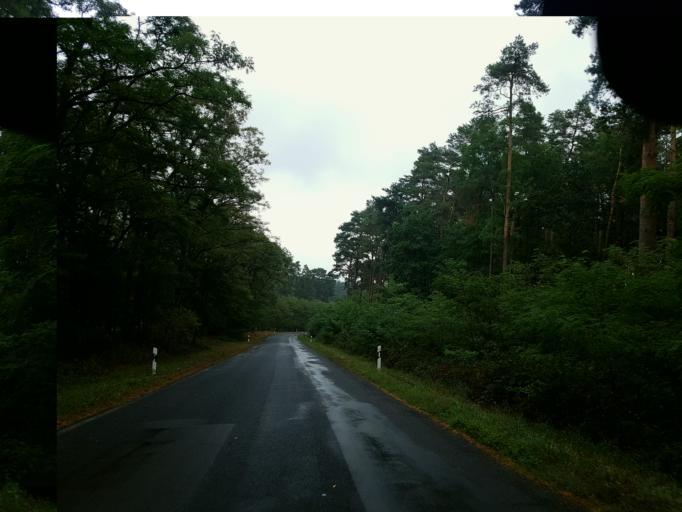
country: DE
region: Brandenburg
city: Gorzke
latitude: 52.1588
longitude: 12.3505
